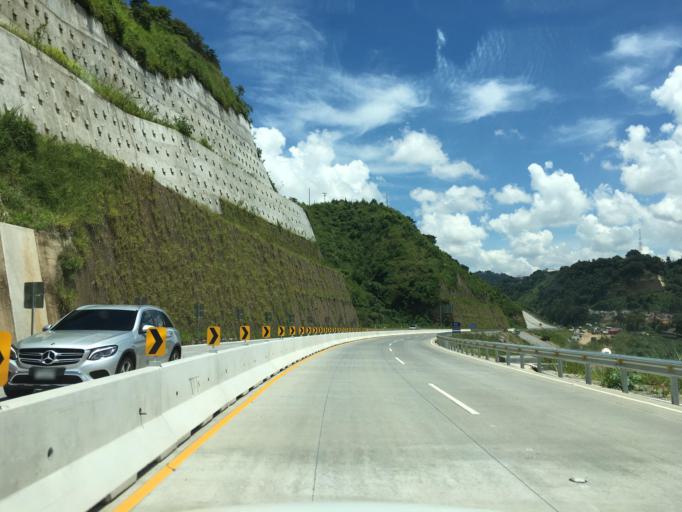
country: GT
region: Guatemala
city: Petapa
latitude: 14.5411
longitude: -90.5347
